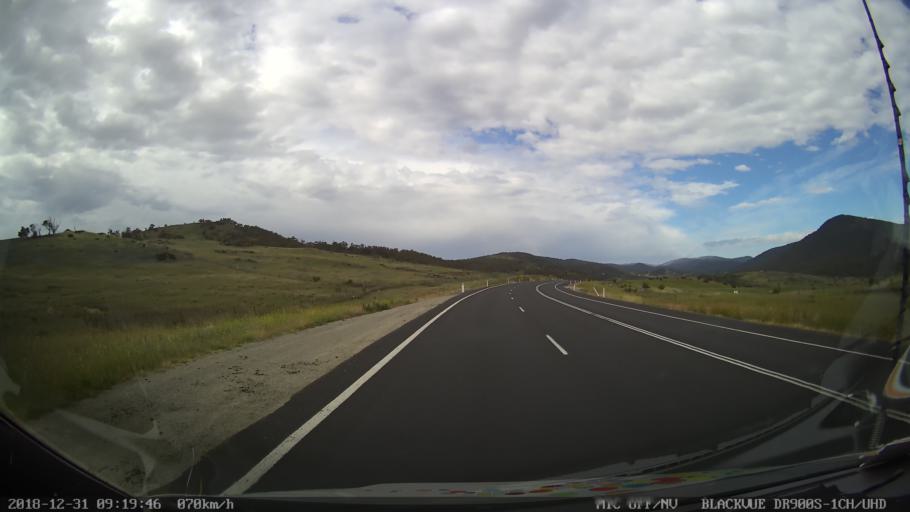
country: AU
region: New South Wales
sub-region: Snowy River
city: Jindabyne
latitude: -36.4173
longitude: 148.5825
